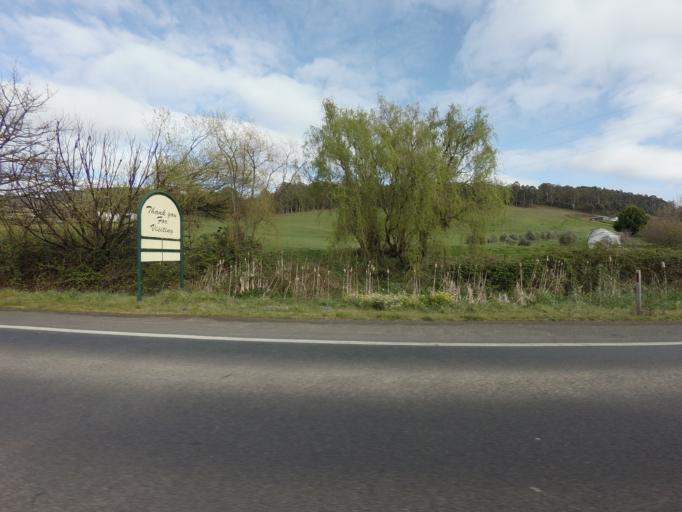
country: AU
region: Tasmania
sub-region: Huon Valley
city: Huonville
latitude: -43.0421
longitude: 147.0445
